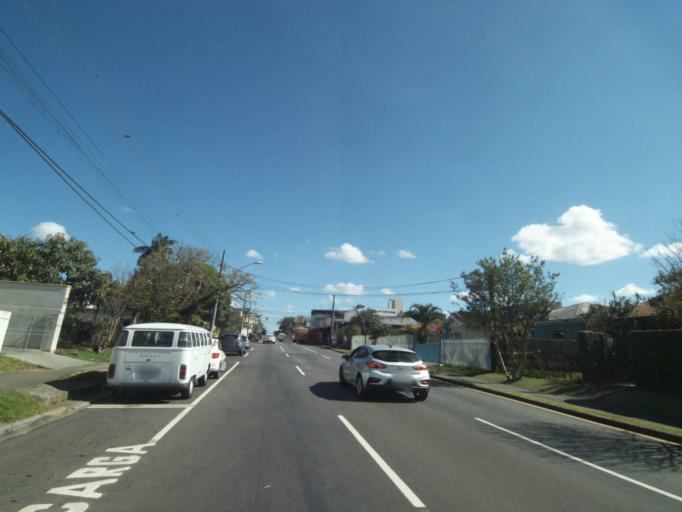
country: BR
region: Parana
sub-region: Curitiba
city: Curitiba
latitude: -25.3988
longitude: -49.2590
